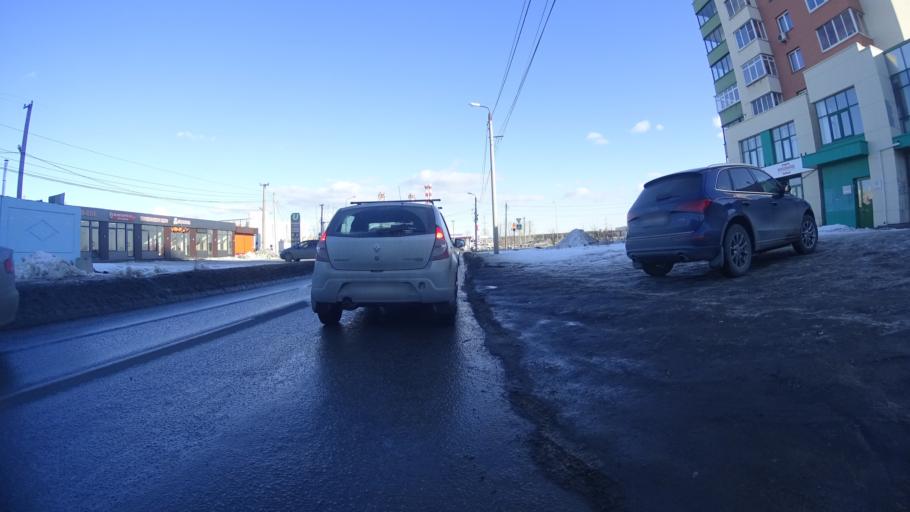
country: RU
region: Chelyabinsk
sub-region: Gorod Chelyabinsk
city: Chelyabinsk
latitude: 55.1670
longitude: 61.3013
